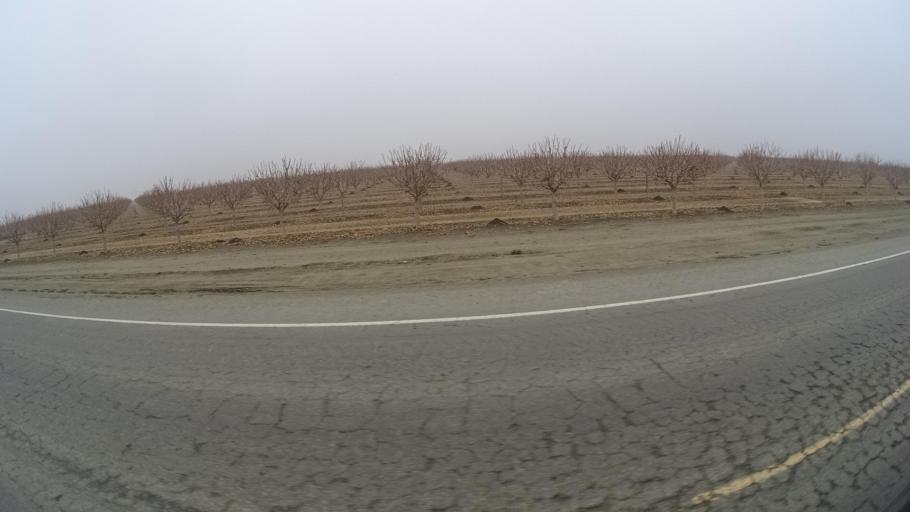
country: US
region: California
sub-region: Kern County
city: Buttonwillow
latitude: 35.4290
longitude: -119.5185
